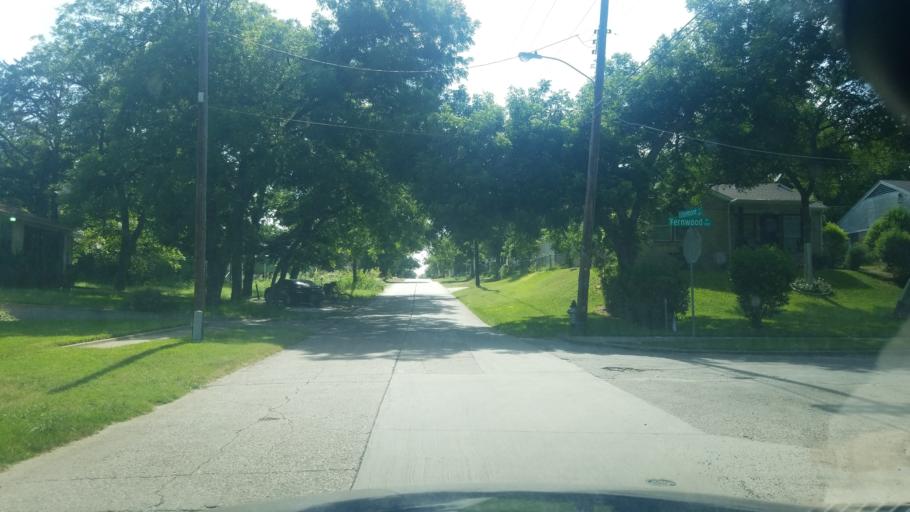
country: US
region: Texas
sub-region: Dallas County
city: Dallas
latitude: 32.7295
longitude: -96.8090
